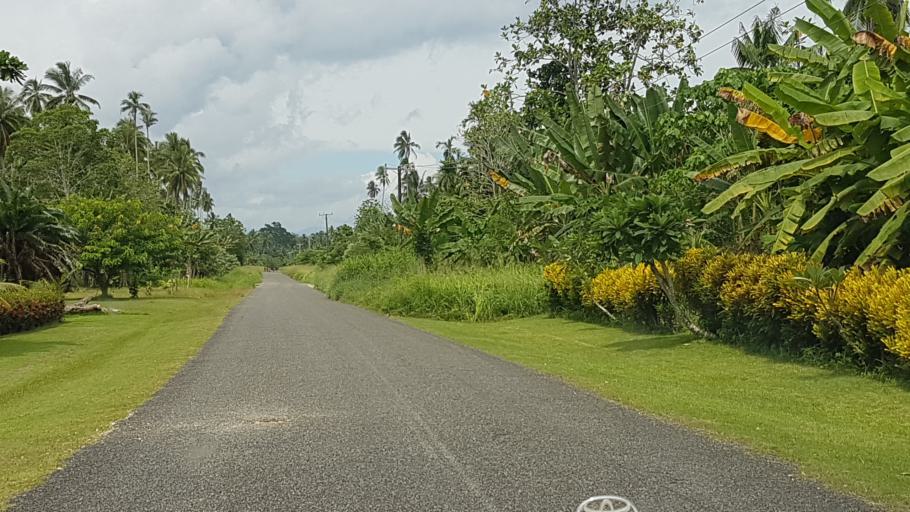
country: PG
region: Madang
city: Madang
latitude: -4.7625
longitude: 145.6819
